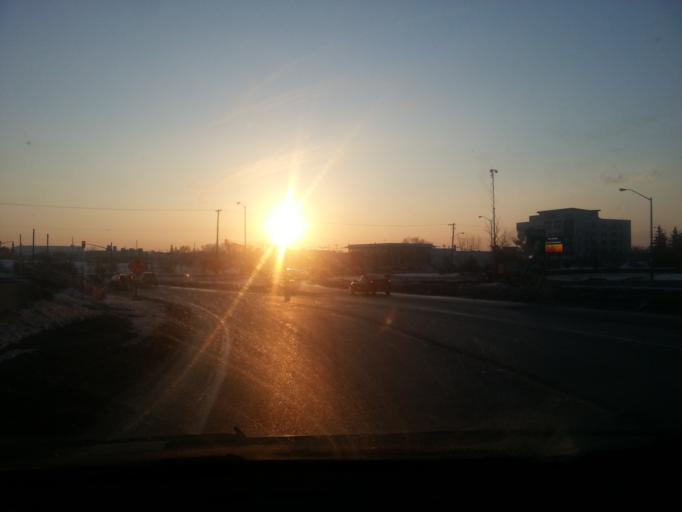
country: CA
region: Ontario
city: Ottawa
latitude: 45.4193
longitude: -75.6359
